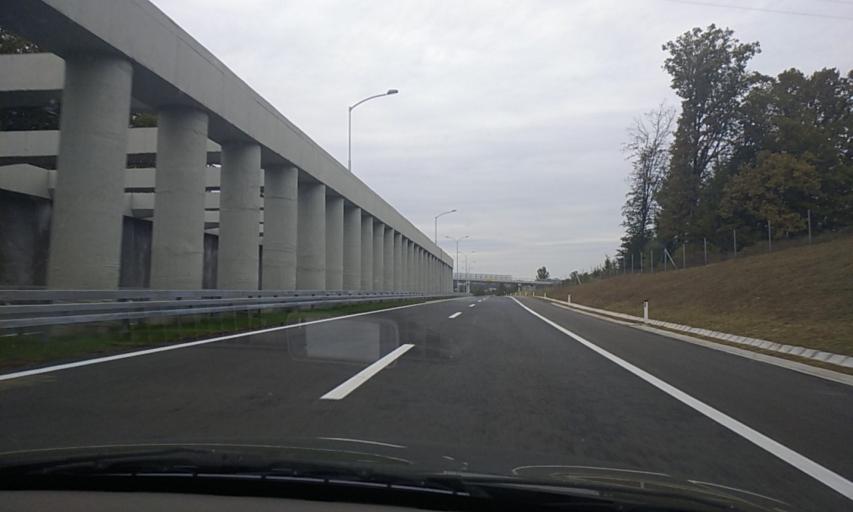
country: BA
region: Republika Srpska
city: Prnjavor
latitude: 44.8673
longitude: 17.6398
